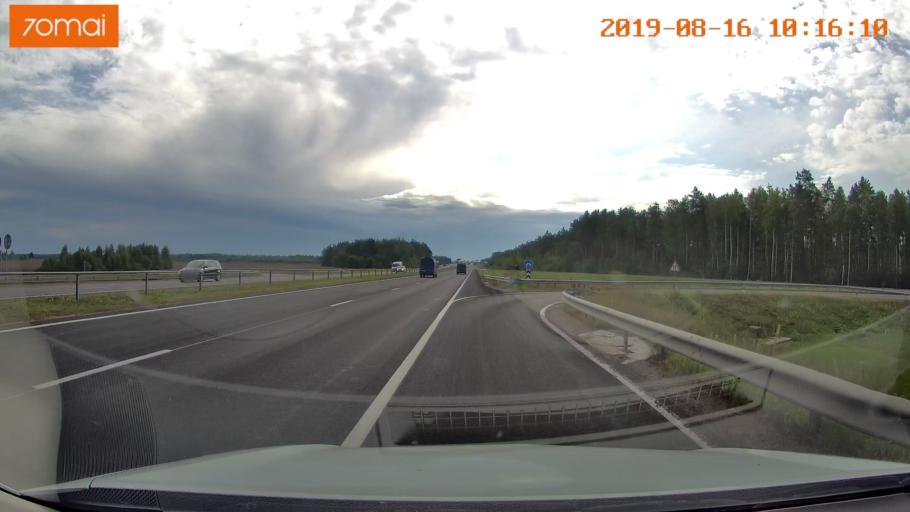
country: BY
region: Mogilev
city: Asipovichy
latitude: 53.3188
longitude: 28.7234
